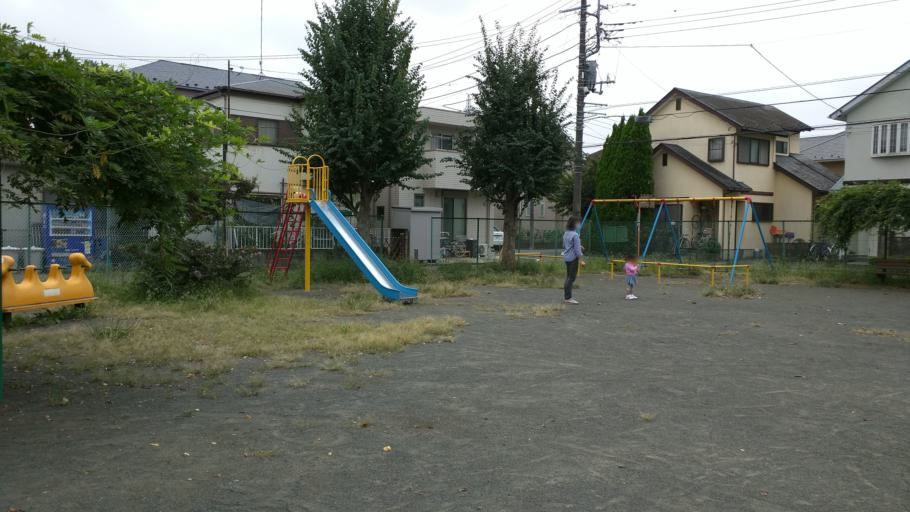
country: JP
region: Tokyo
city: Chofugaoka
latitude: 35.6840
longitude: 139.5179
